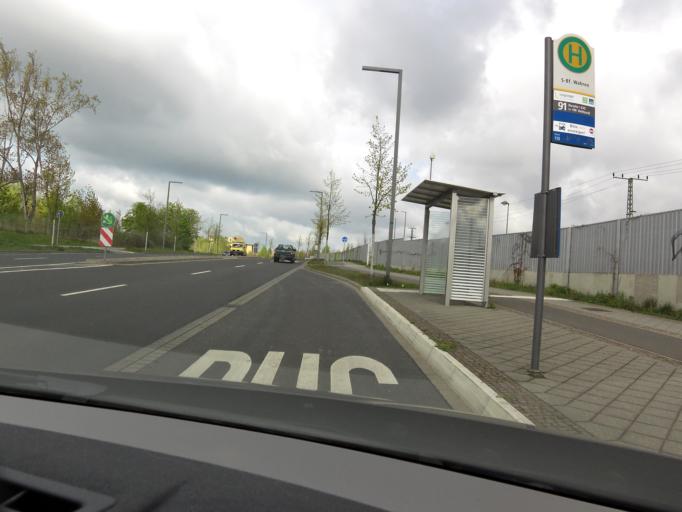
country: DE
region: Saxony
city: Leipzig
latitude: 51.3800
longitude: 12.3222
